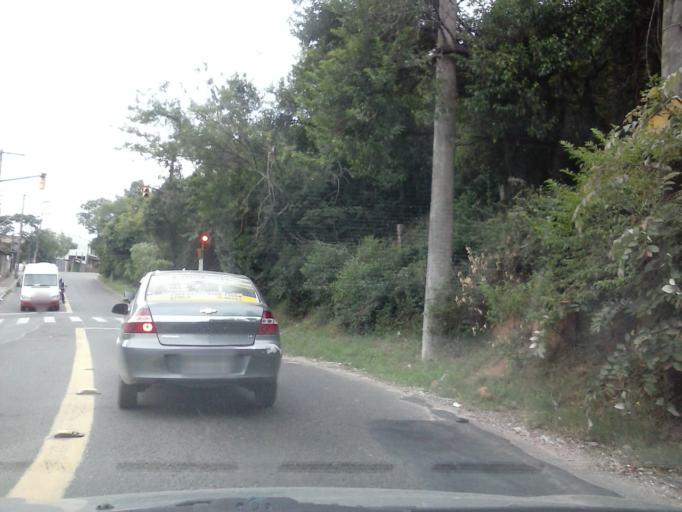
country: BR
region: Rio Grande do Sul
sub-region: Porto Alegre
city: Porto Alegre
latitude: -30.0911
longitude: -51.1818
